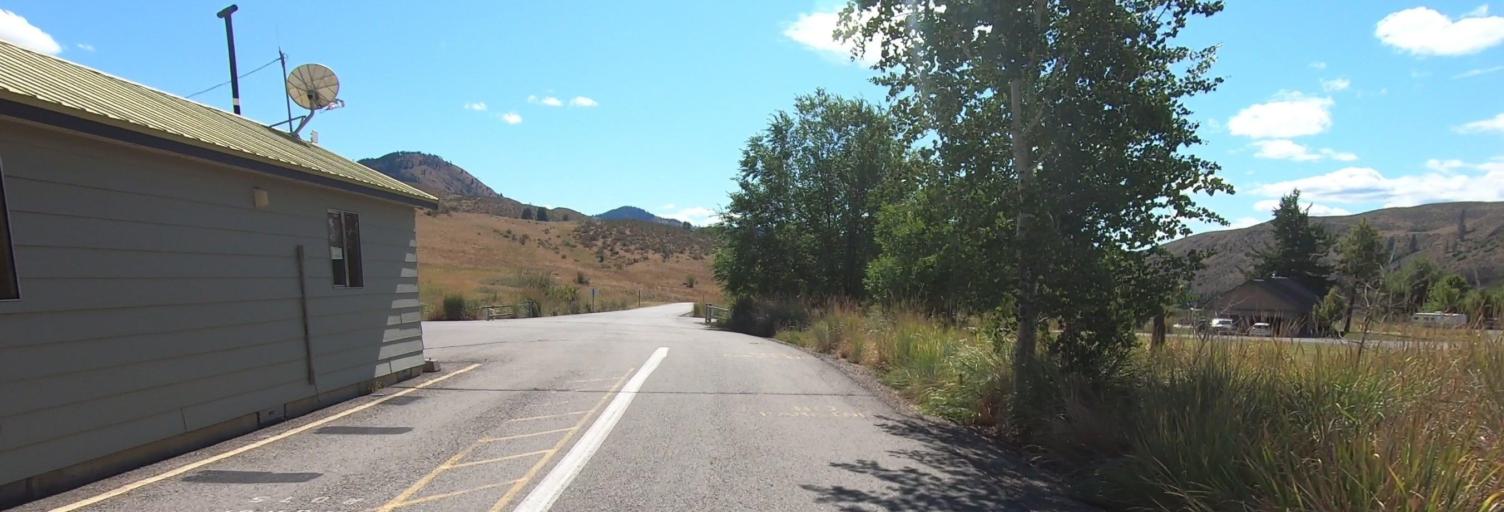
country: US
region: Washington
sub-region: Okanogan County
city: Brewster
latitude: 48.4912
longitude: -120.1421
